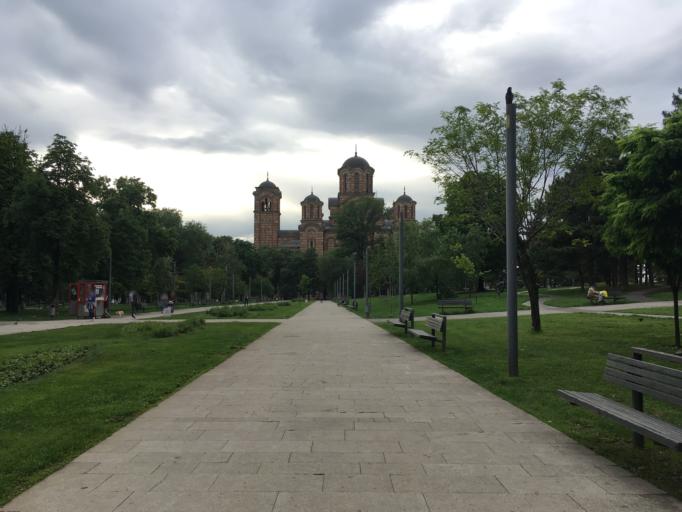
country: RS
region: Central Serbia
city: Belgrade
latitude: 44.8092
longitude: 20.4710
